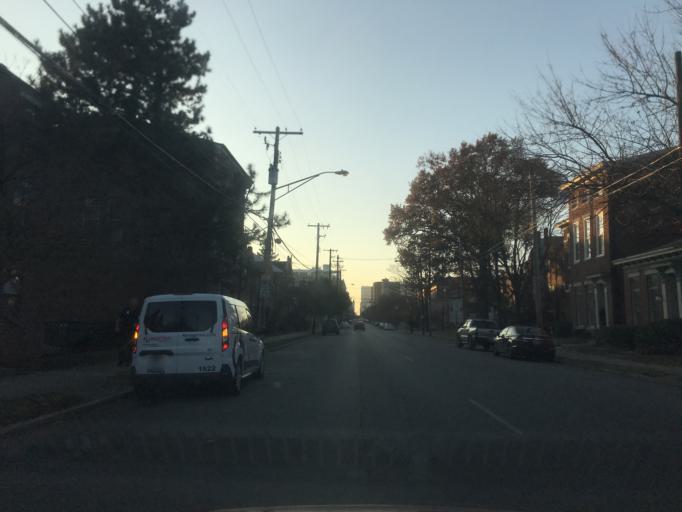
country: US
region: Kentucky
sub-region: Jefferson County
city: Louisville
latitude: 38.2490
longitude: -85.7375
